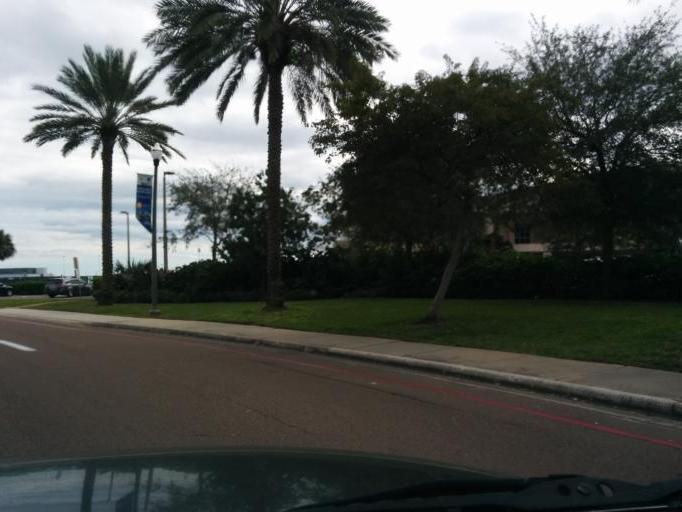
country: US
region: Florida
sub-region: Pinellas County
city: Saint Petersburg
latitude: 27.7654
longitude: -82.6333
